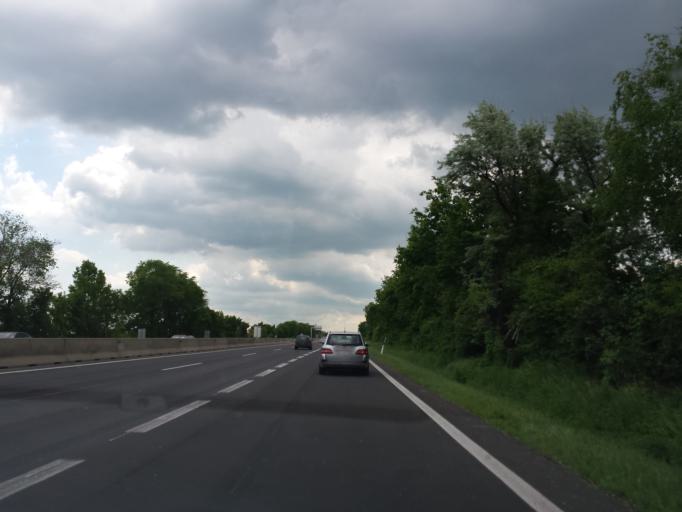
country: AT
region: Lower Austria
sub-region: Politischer Bezirk Wien-Umgebung
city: Fischamend Dorf
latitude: 48.1150
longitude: 16.6311
